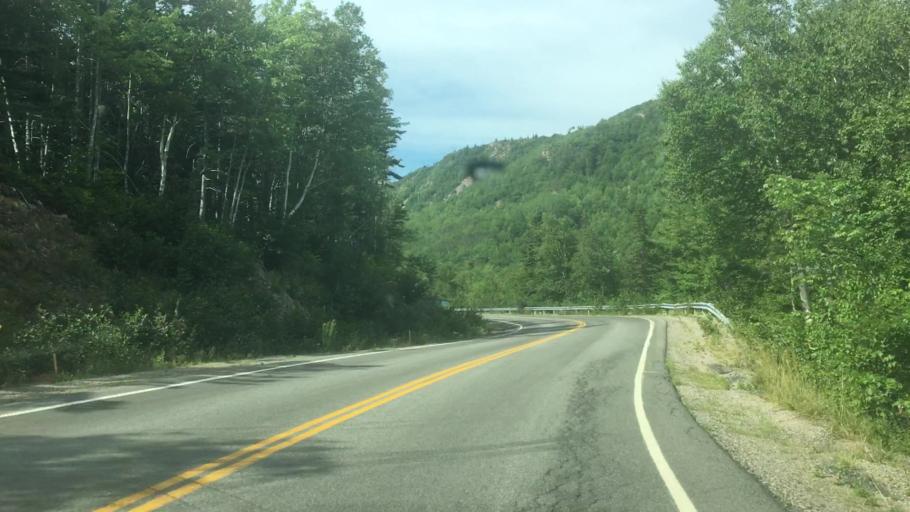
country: CA
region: Nova Scotia
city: Sydney Mines
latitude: 46.5807
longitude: -60.3912
